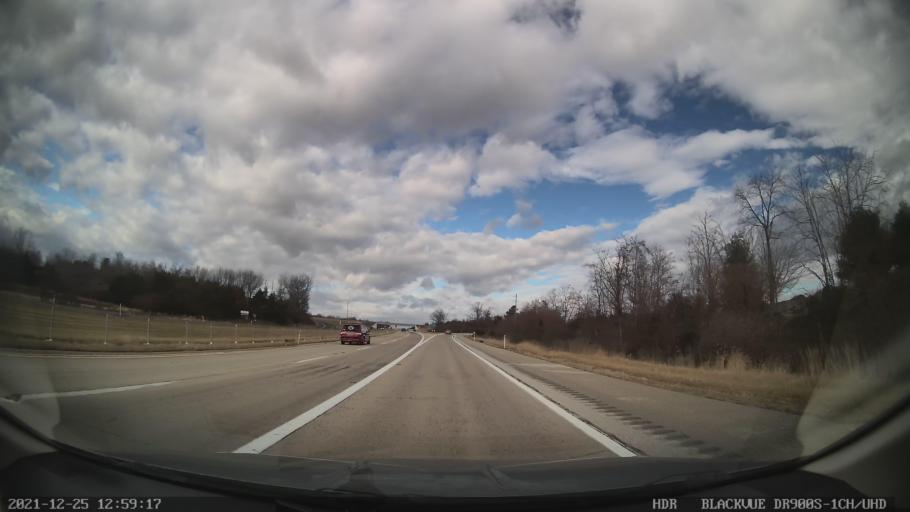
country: US
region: Pennsylvania
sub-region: Adams County
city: Lake Heritage
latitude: 39.8421
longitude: -77.1941
